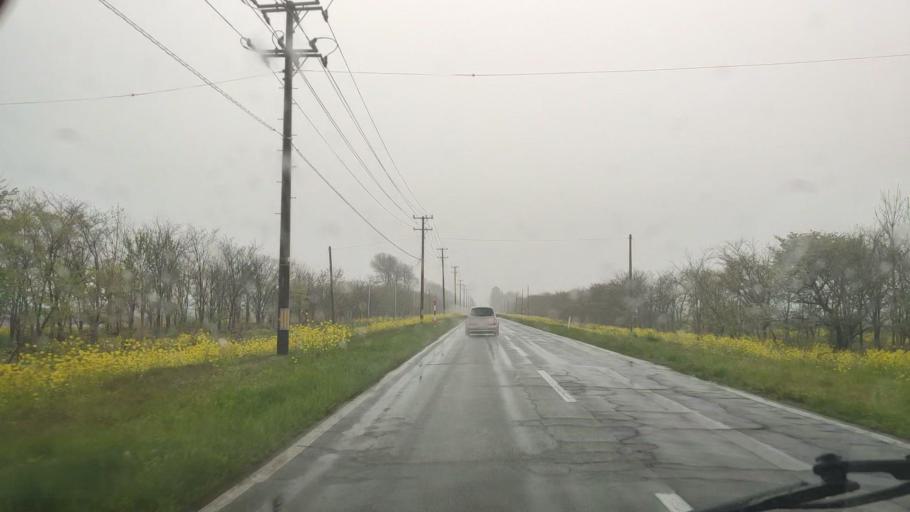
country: JP
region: Akita
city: Tenno
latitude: 39.9814
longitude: 139.9463
